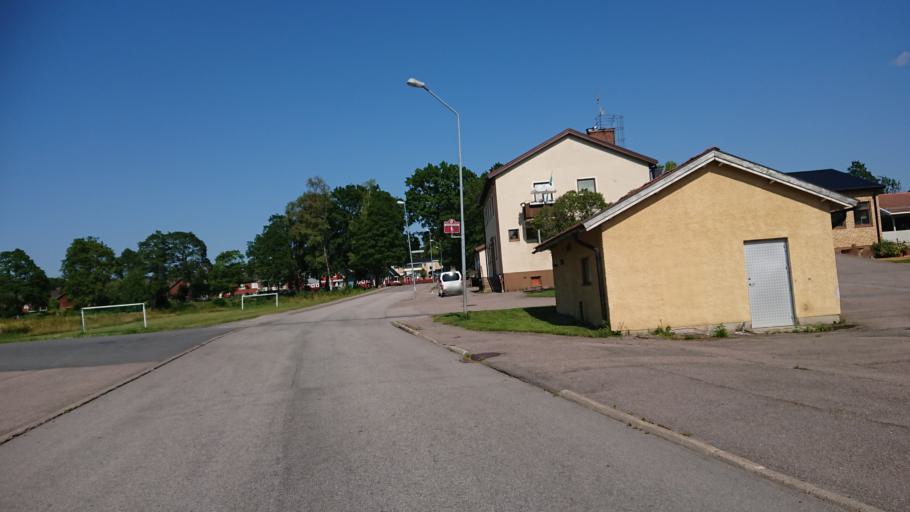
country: SE
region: Uppsala
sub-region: Osthammars Kommun
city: Osterbybruk
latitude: 60.1966
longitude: 17.8999
